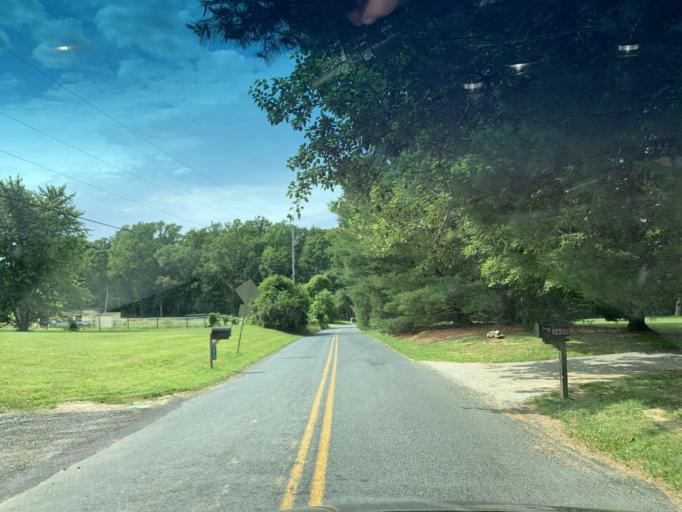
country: US
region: Maryland
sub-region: Harford County
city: Jarrettsville
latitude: 39.6046
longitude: -76.4606
